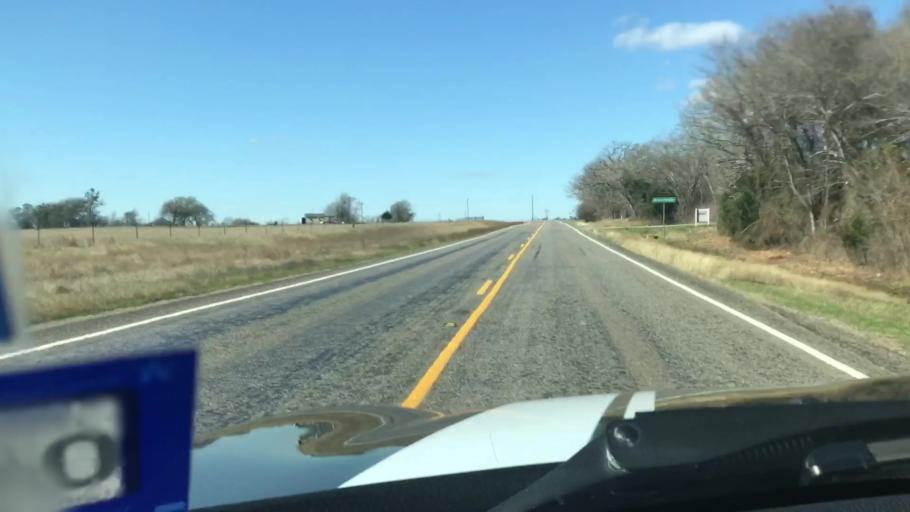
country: US
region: Texas
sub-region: Robertson County
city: Calvert
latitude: 30.8835
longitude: -96.7491
